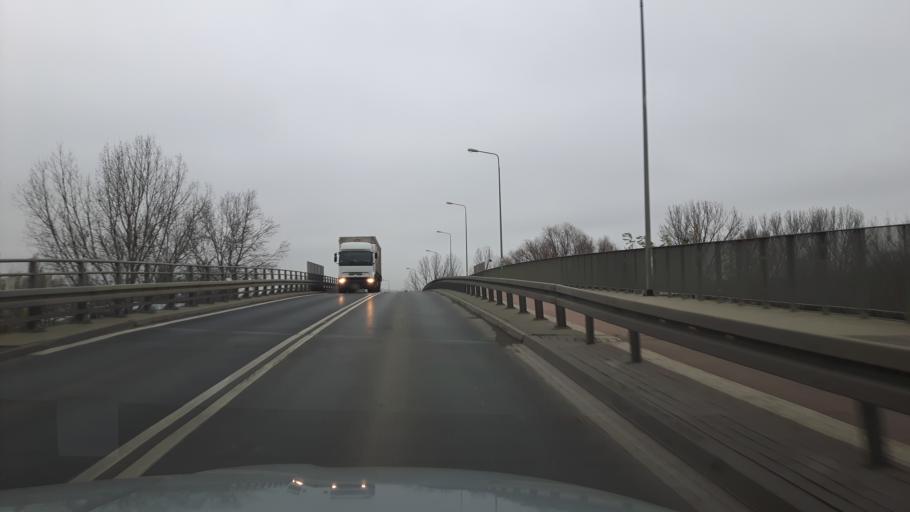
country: PL
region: Masovian Voivodeship
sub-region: Warszawa
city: Praga Poludnie
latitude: 52.2705
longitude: 21.0702
